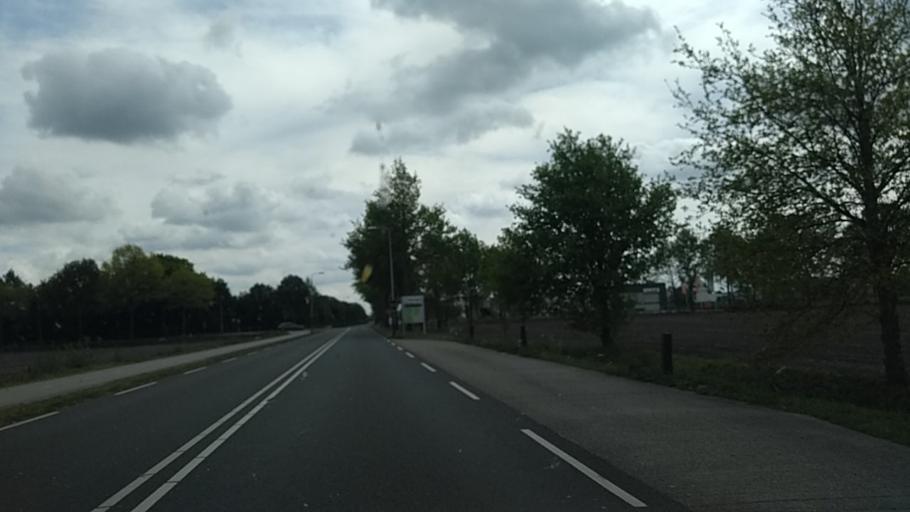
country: NL
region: Overijssel
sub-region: Gemeente Staphorst
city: Staphorst
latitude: 52.6388
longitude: 6.2059
